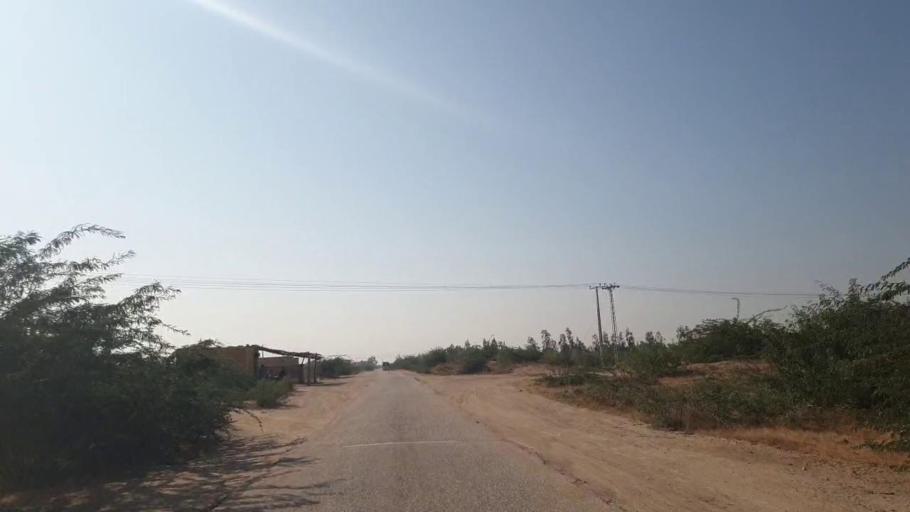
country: PK
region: Sindh
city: Thatta
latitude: 25.1512
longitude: 67.7738
